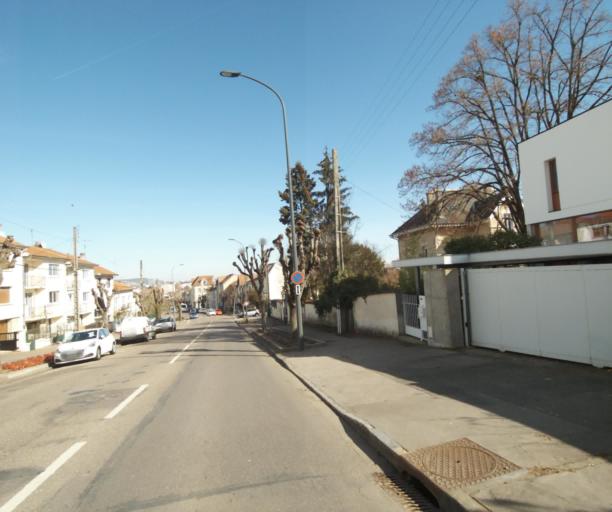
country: FR
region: Lorraine
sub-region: Departement de Meurthe-et-Moselle
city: Villers-les-Nancy
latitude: 48.6729
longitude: 6.1478
